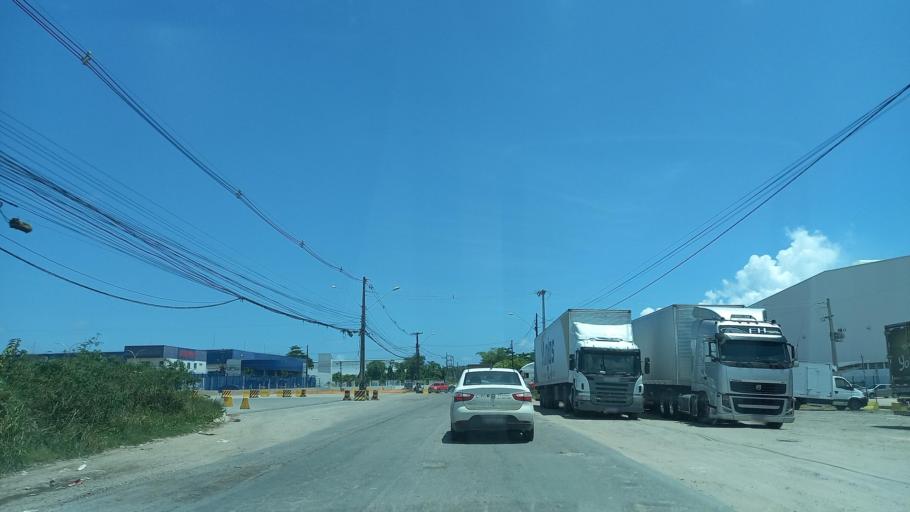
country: BR
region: Pernambuco
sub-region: Jaboatao Dos Guararapes
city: Jaboatao
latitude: -8.1550
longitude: -34.9623
